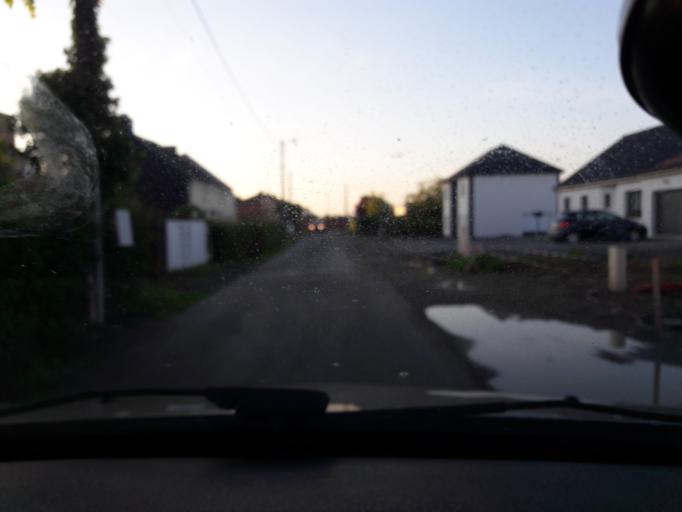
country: FR
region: Nord-Pas-de-Calais
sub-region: Departement du Nord
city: Recquignies
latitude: 50.2774
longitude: 4.0461
